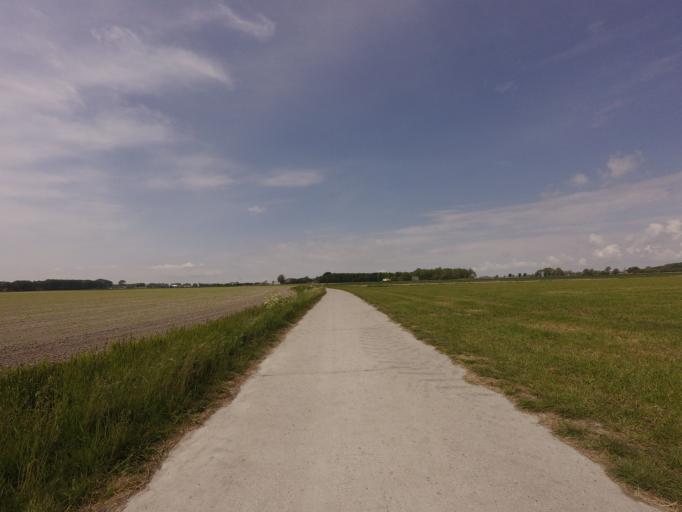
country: NL
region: Friesland
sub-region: Sudwest Fryslan
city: Bolsward
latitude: 53.1064
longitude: 5.4882
